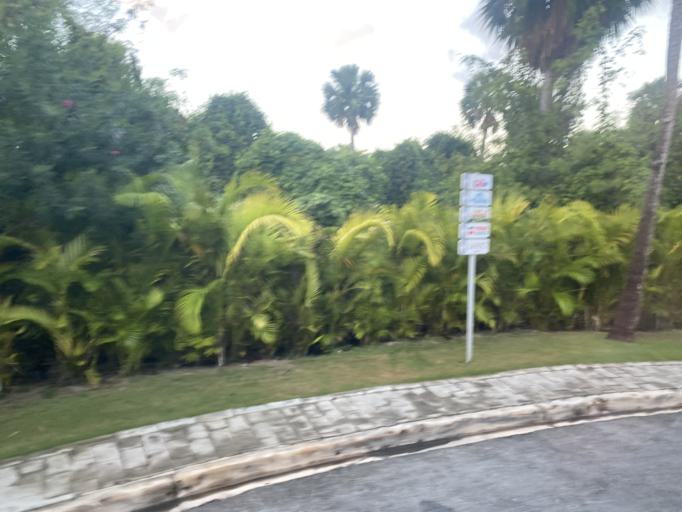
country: DO
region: San Juan
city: Punta Cana
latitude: 18.7219
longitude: -68.4599
